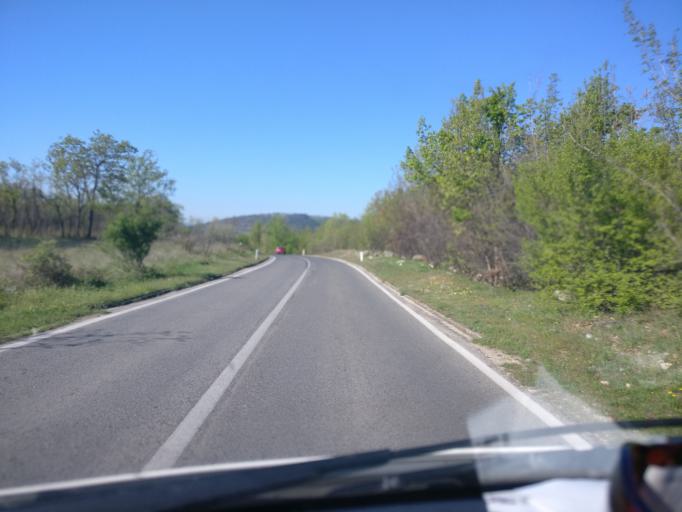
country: BA
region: Federation of Bosnia and Herzegovina
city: Tasovcici
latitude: 43.1298
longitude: 17.7660
